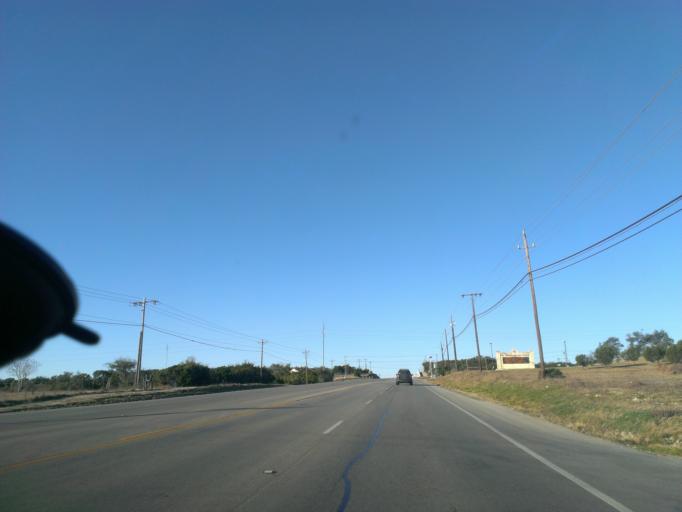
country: US
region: Texas
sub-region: Travis County
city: Bee Cave
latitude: 30.2260
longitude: -97.9472
